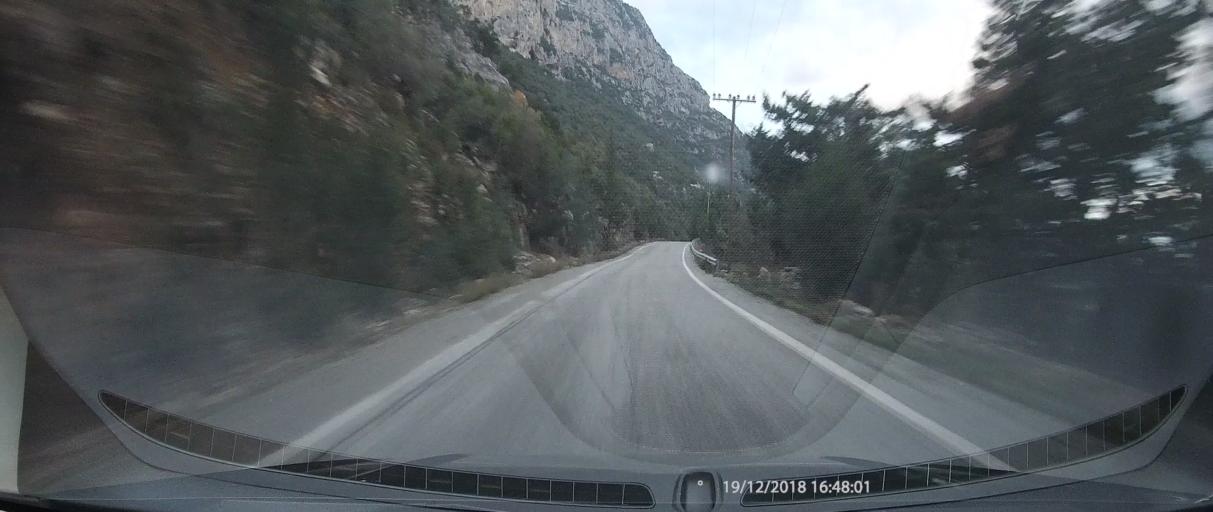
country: GR
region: Peloponnese
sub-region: Nomos Lakonias
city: Sykea
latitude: 36.9328
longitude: 23.0010
